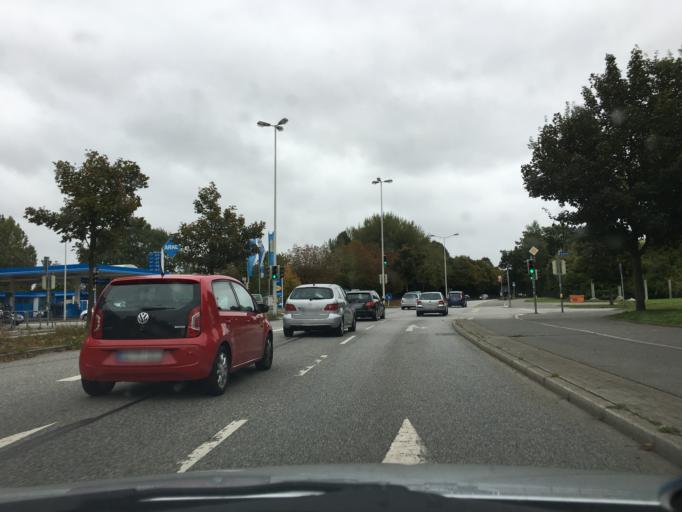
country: DE
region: Schleswig-Holstein
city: Ottendorf
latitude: 54.3258
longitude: 10.0571
